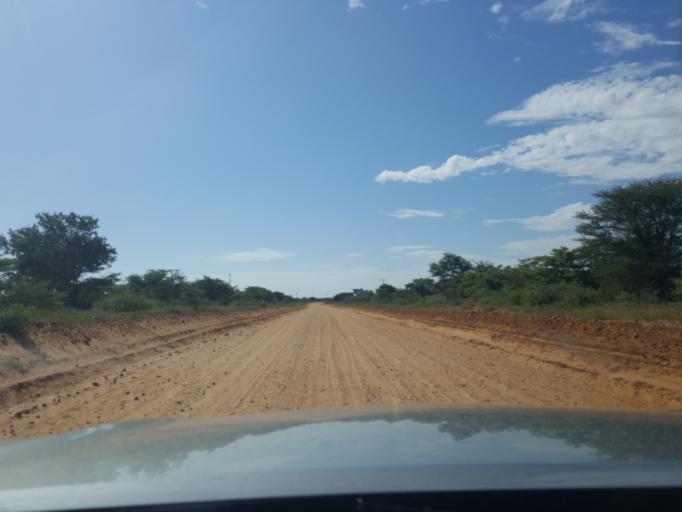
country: BW
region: Kweneng
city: Khudumelapye
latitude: -23.7051
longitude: 24.7245
